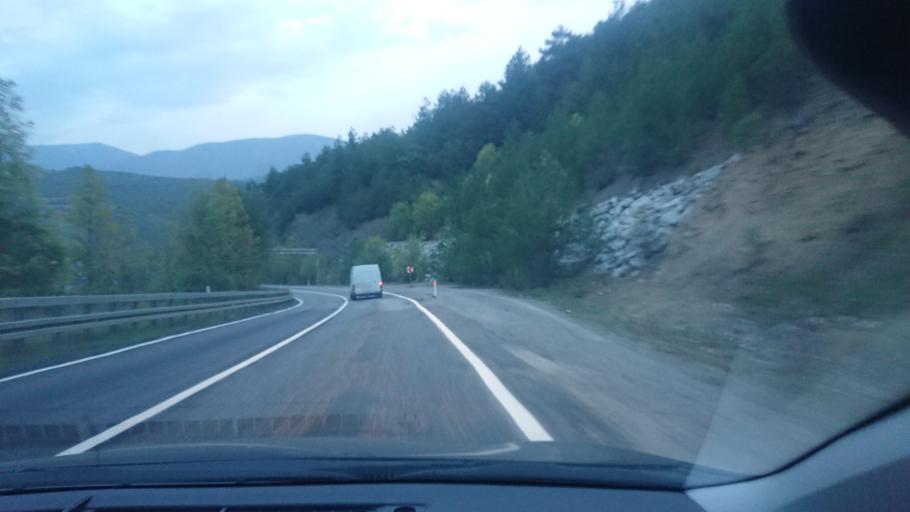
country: TR
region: Karabuk
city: Karabuk
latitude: 41.1582
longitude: 32.5443
